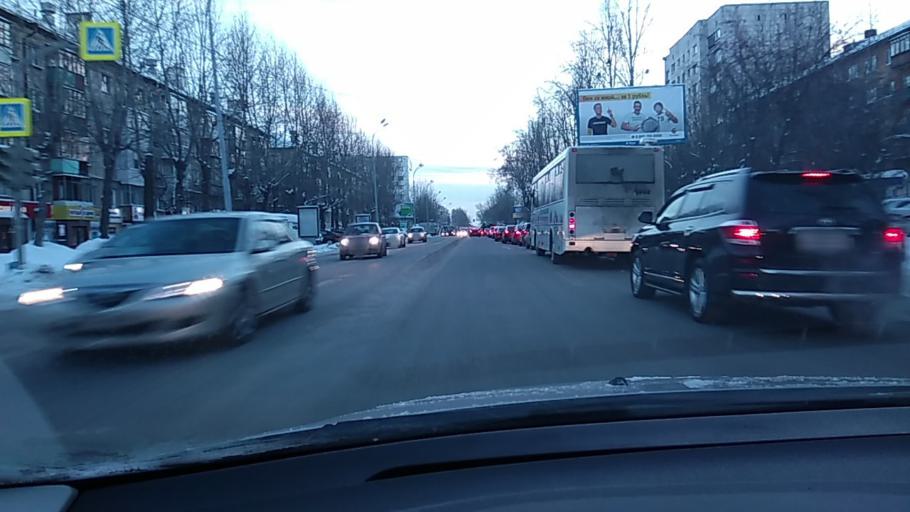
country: RU
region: Sverdlovsk
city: Yekaterinburg
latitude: 56.8288
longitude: 60.6368
